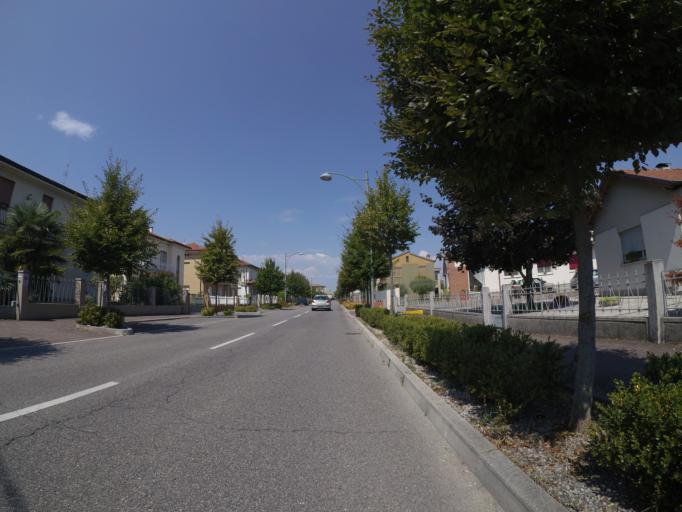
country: IT
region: Friuli Venezia Giulia
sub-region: Provincia di Udine
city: Codroipo
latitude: 45.9573
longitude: 12.9847
